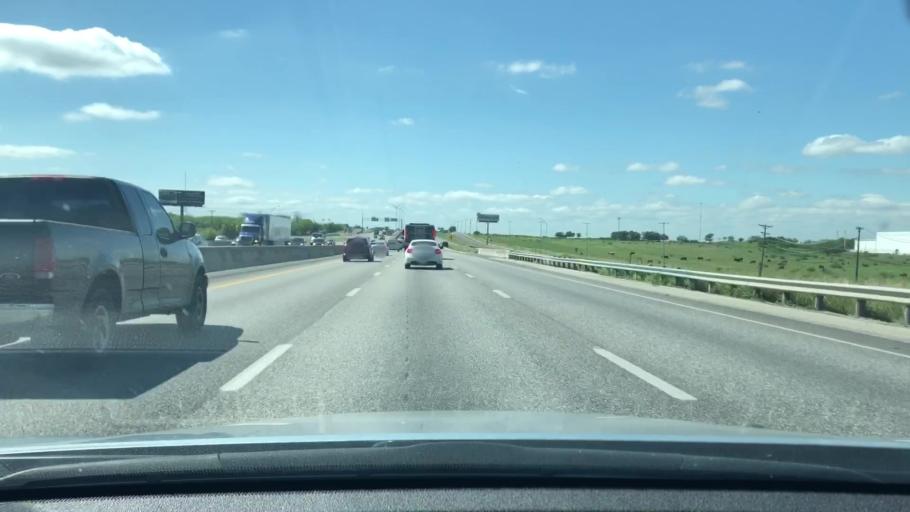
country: US
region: Texas
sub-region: Guadalupe County
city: Northcliff
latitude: 29.6402
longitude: -98.2109
